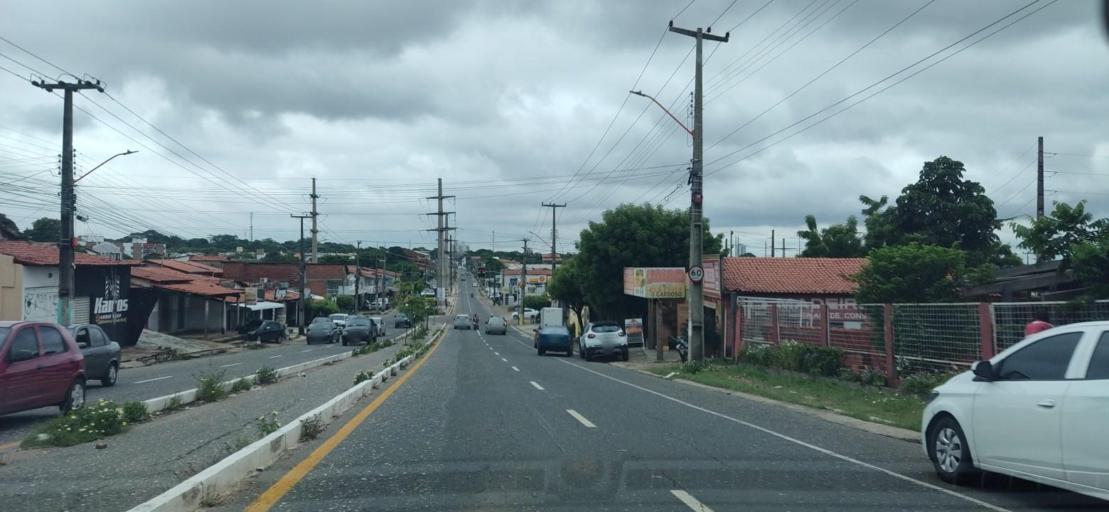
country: BR
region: Piaui
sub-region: Teresina
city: Teresina
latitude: -5.0580
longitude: -42.7506
